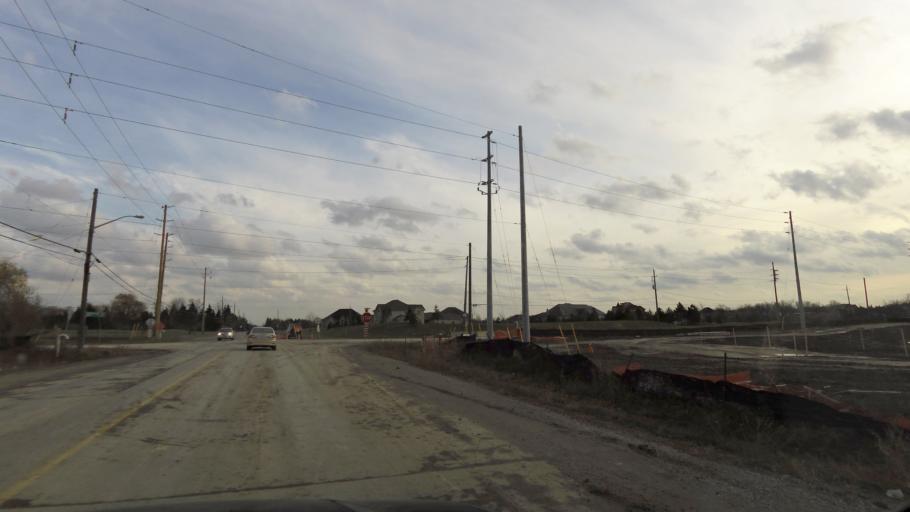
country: CA
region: Ontario
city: Brampton
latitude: 43.8026
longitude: -79.7276
